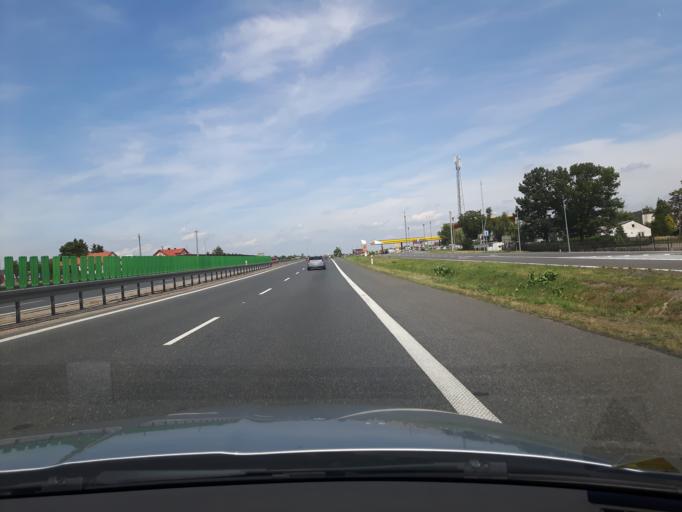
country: PL
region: Masovian Voivodeship
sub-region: Powiat plonski
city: Zaluski
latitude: 52.5118
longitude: 20.5287
